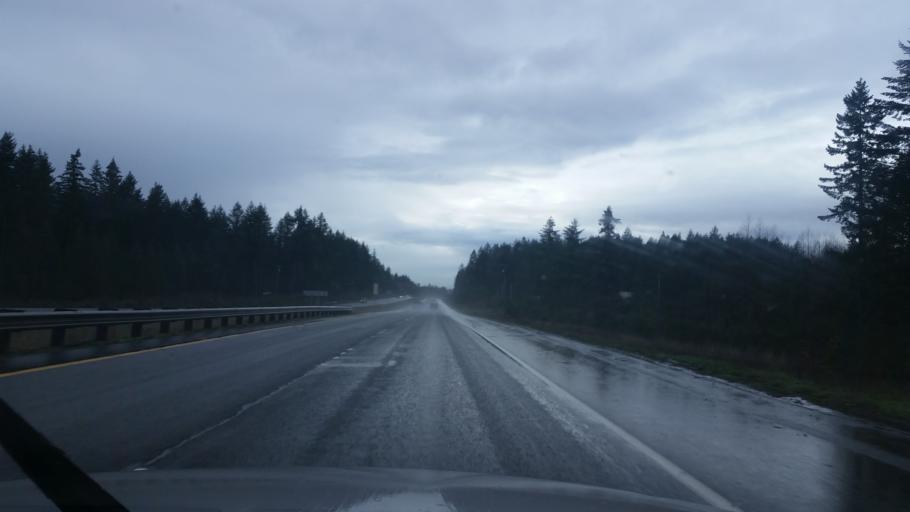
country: US
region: Washington
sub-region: King County
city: Maple Valley
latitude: 47.3860
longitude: -122.0618
